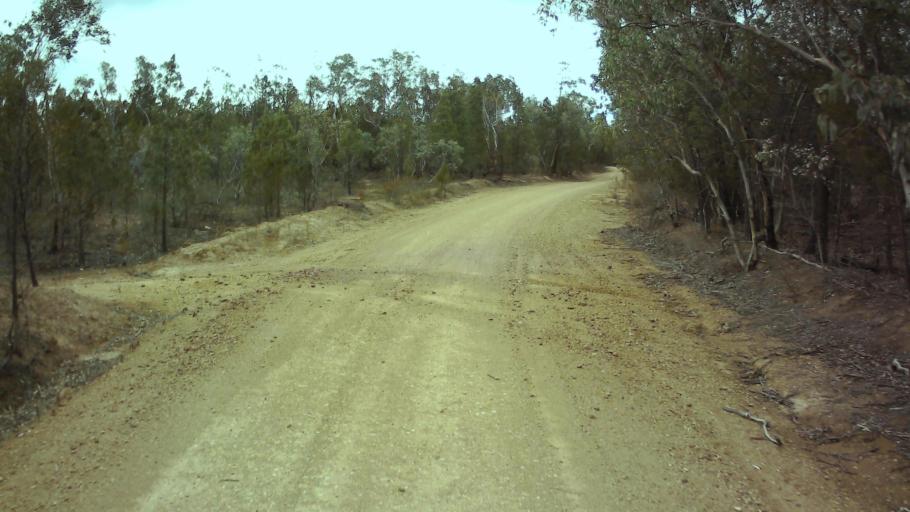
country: AU
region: New South Wales
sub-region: Weddin
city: Grenfell
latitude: -33.8853
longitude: 148.1576
